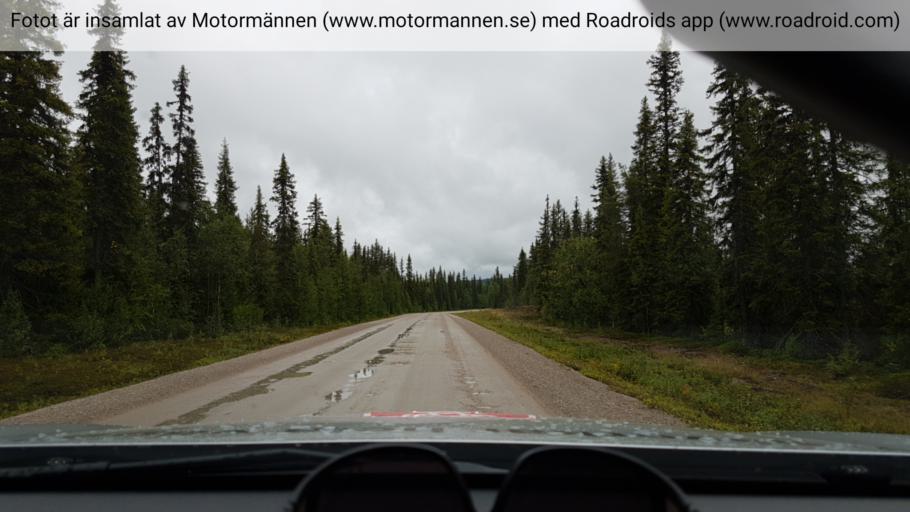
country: SE
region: Vaesterbotten
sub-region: Storumans Kommun
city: Storuman
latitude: 64.8815
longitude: 17.3222
